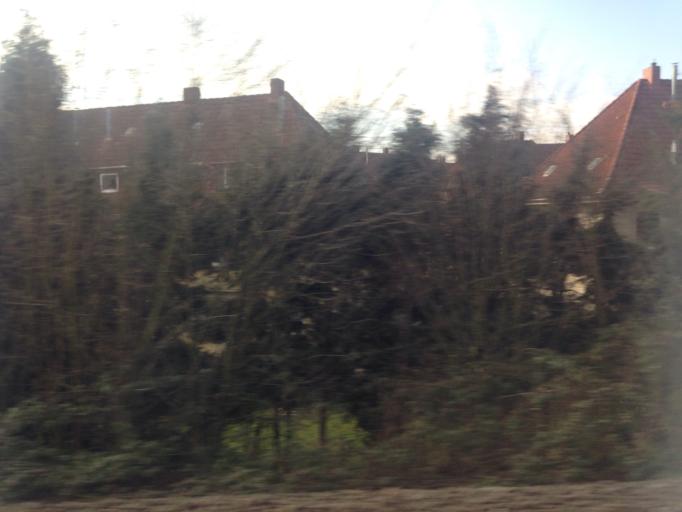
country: DE
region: North Rhine-Westphalia
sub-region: Regierungsbezirk Munster
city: Muenster
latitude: 51.9698
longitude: 7.6447
